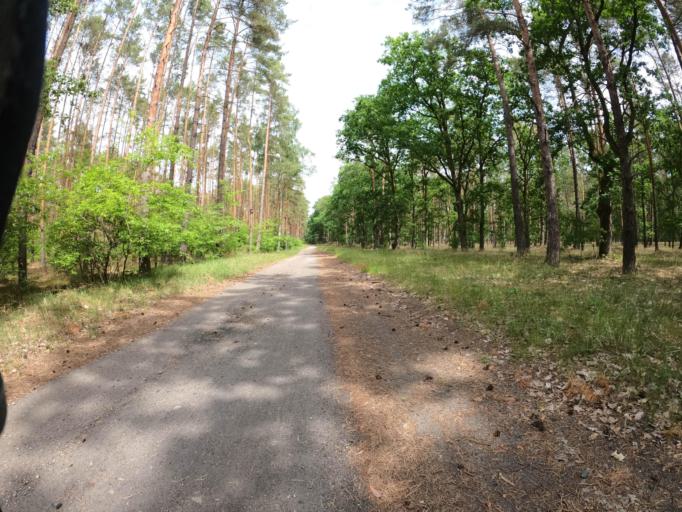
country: DE
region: Brandenburg
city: Zechin
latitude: 52.6832
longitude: 14.4911
